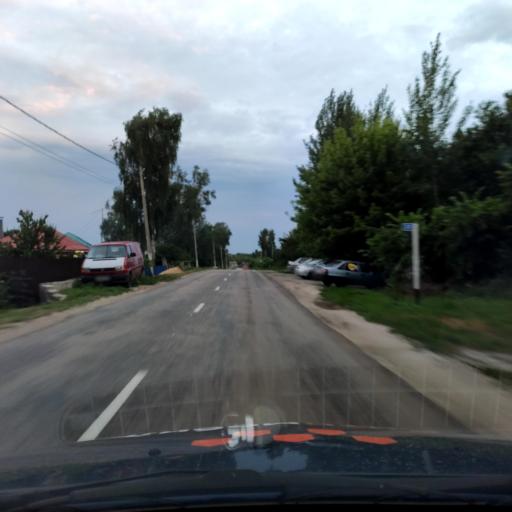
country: RU
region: Voronezj
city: Shilovo
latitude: 51.5001
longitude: 39.0108
